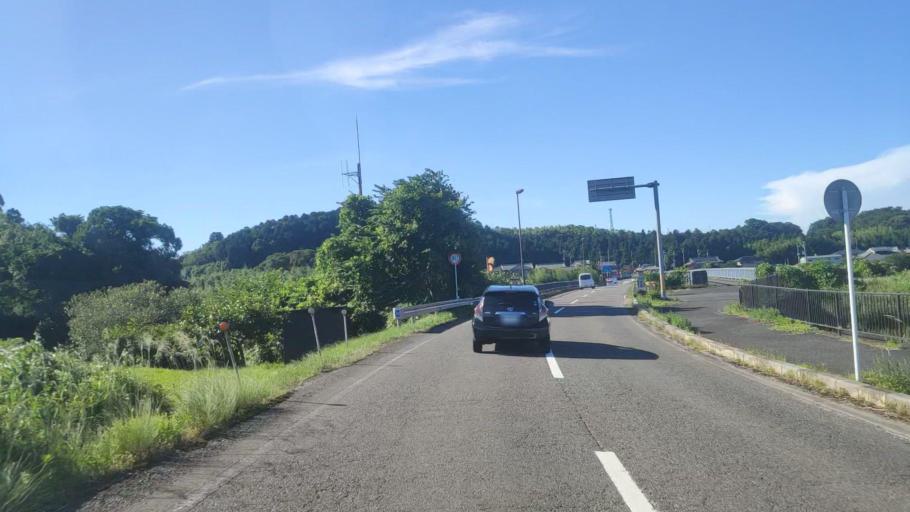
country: JP
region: Shiga Prefecture
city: Minakuchicho-matoba
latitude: 34.9555
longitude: 136.2019
